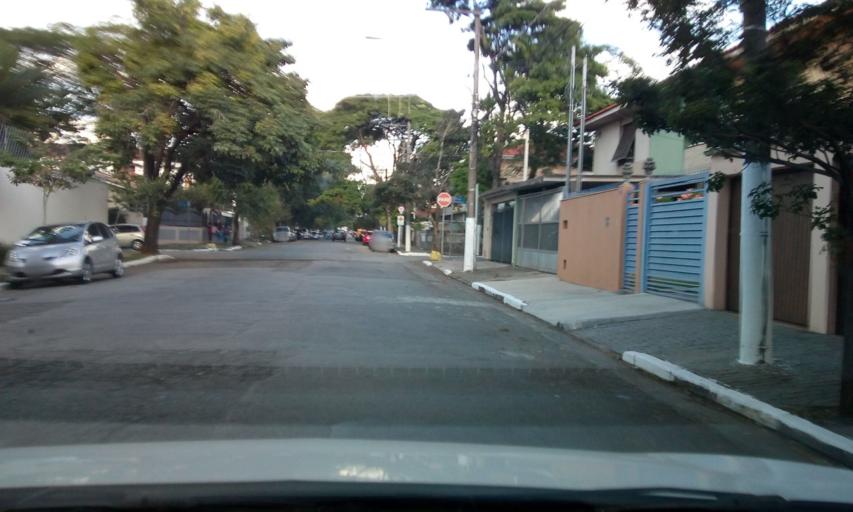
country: BR
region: Sao Paulo
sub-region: Sao Paulo
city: Sao Paulo
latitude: -23.6178
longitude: -46.6892
